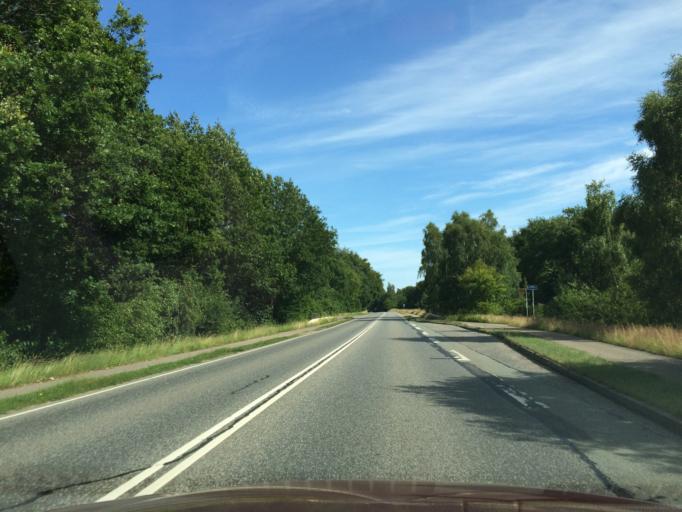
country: DK
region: Central Jutland
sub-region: Silkeborg Kommune
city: Silkeborg
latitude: 56.1928
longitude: 9.5306
